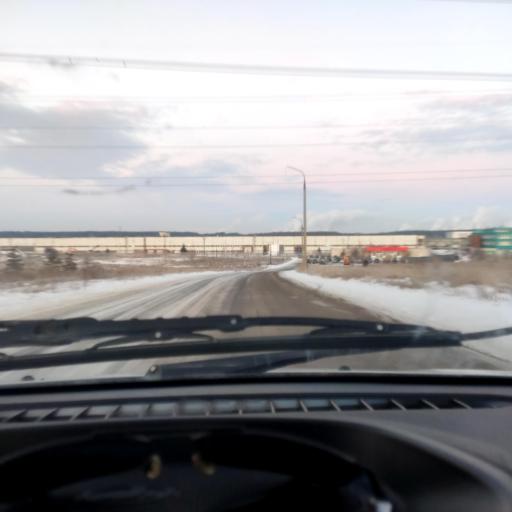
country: RU
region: Samara
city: Zhigulevsk
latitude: 53.5142
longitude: 49.5294
